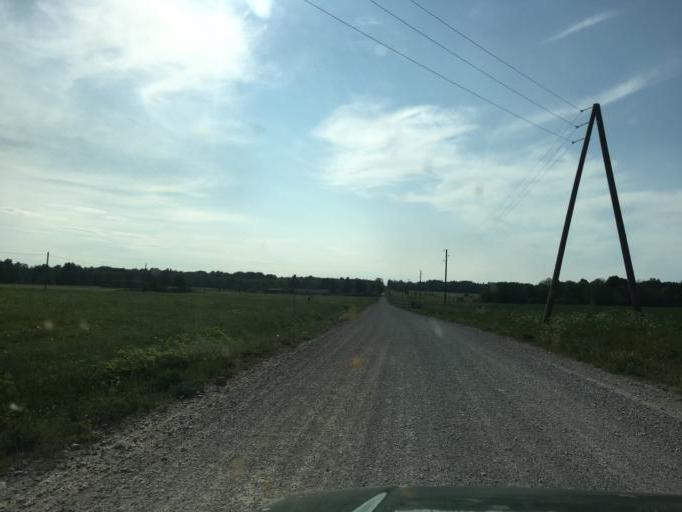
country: LV
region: Dundaga
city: Dundaga
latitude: 57.6234
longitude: 22.4031
